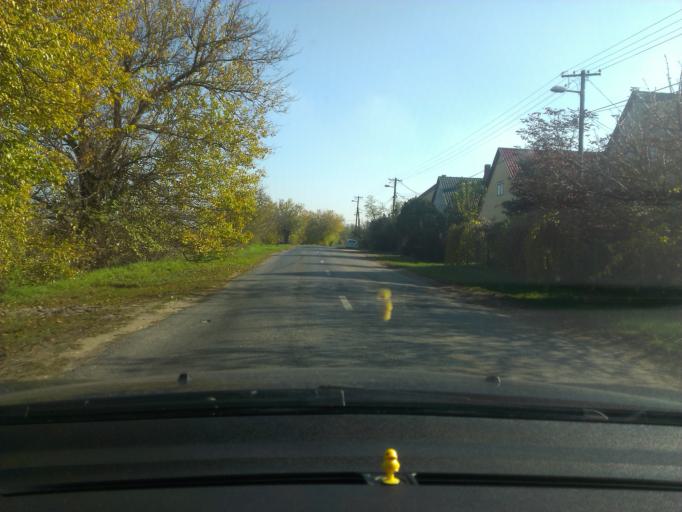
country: HU
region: Komarom-Esztergom
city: Komarom
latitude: 47.7237
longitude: 18.1661
